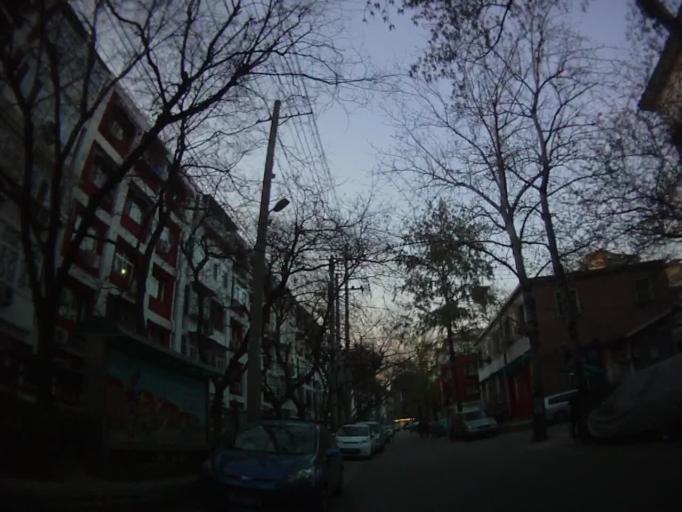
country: CN
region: Beijing
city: Longtan
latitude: 39.8858
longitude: 116.4293
